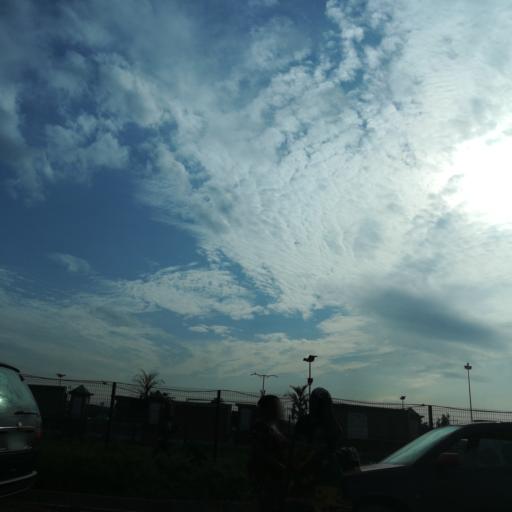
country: NG
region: Lagos
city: Oshodi
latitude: 6.5629
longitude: 3.3489
